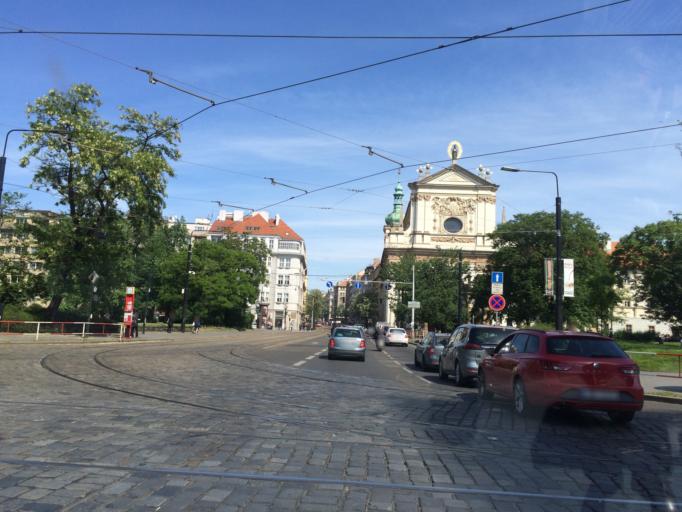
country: CZ
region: Praha
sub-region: Praha 2
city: Vysehrad
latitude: 50.0758
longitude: 14.4190
